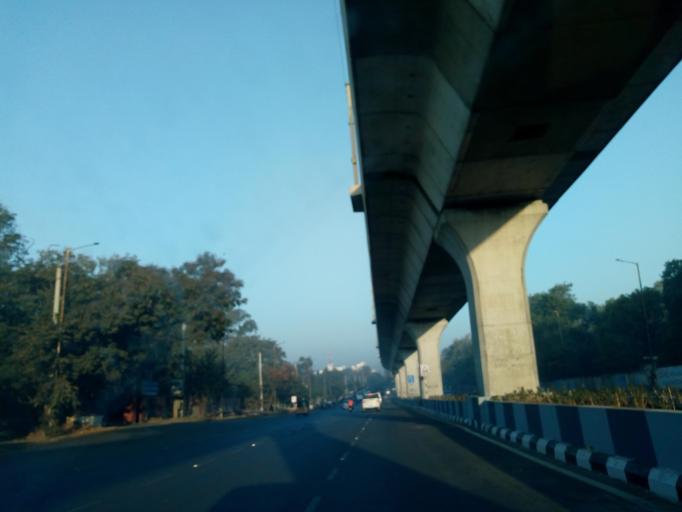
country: IN
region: Telangana
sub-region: Hyderabad
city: Malkajgiri
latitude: 17.4324
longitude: 78.5232
